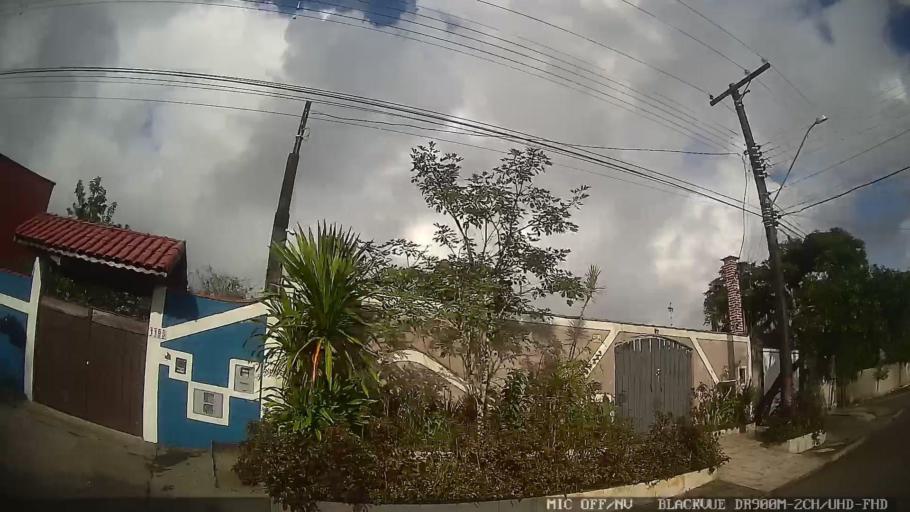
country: BR
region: Sao Paulo
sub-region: Itanhaem
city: Itanhaem
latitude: -24.1883
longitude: -46.8608
